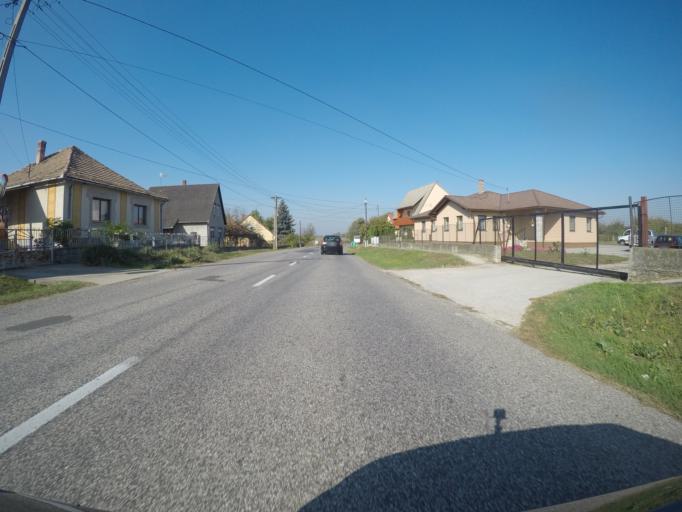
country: HU
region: Tolna
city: Szedres
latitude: 46.4872
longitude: 18.6800
